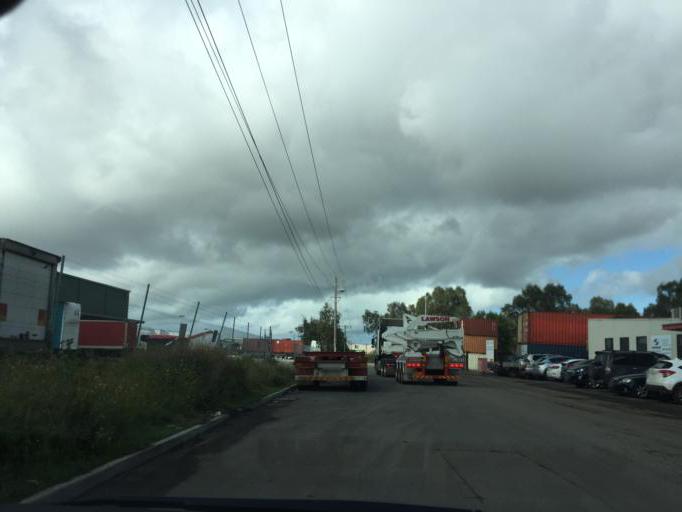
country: AU
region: Victoria
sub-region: Maribyrnong
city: Braybrook
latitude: -37.8017
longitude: 144.8531
